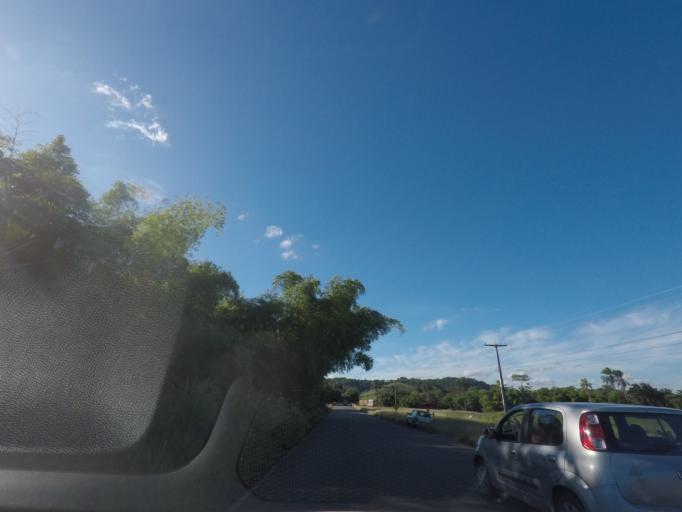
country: BR
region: Bahia
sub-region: Nazare
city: Nazare
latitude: -13.0631
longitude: -39.0052
